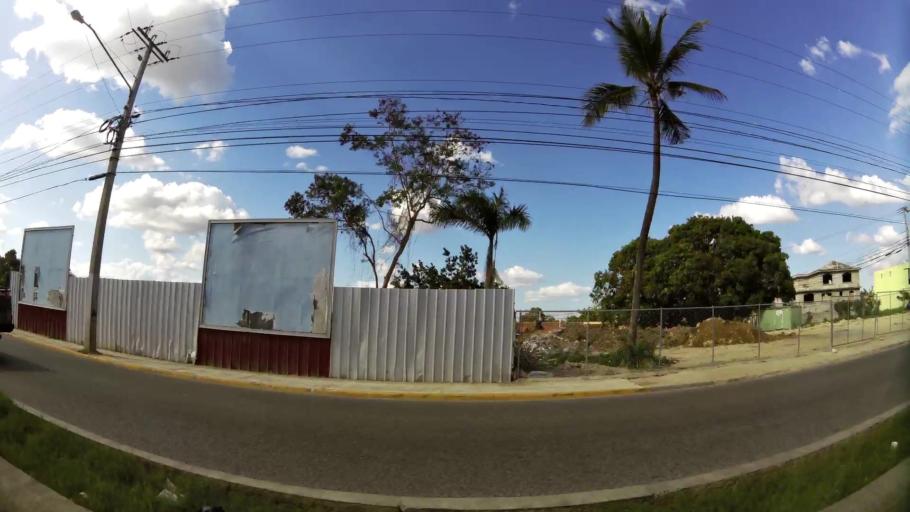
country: DO
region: Nacional
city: Santo Domingo
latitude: 18.5074
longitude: -69.9926
